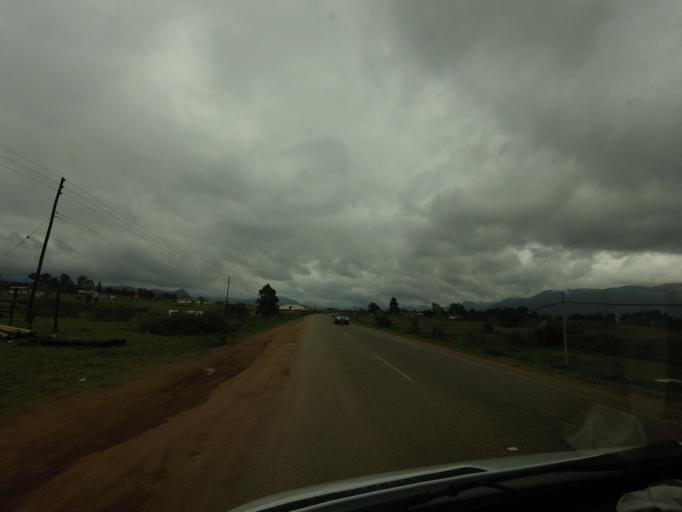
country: SZ
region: Hhohho
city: Lobamba
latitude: -26.4881
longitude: 31.2234
